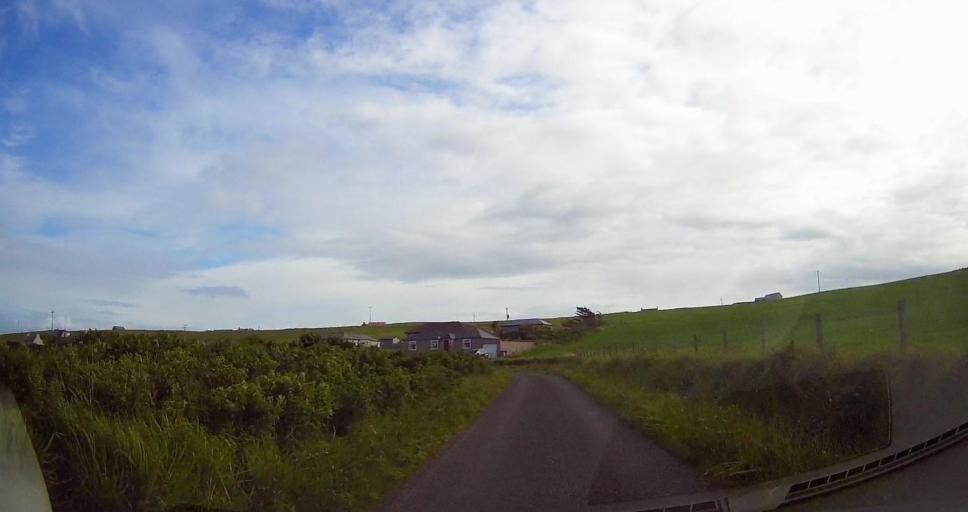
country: GB
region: Scotland
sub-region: Orkney Islands
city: Stromness
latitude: 58.7824
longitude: -3.2348
